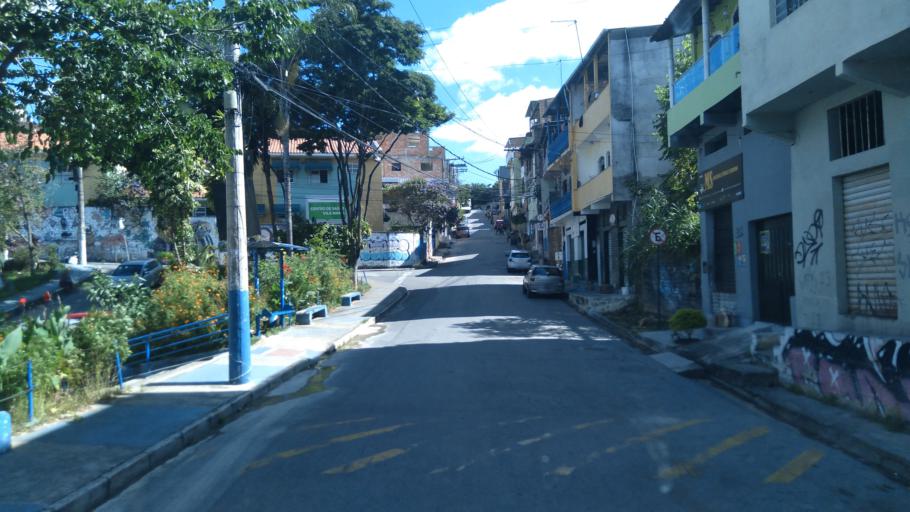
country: BR
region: Minas Gerais
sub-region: Belo Horizonte
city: Belo Horizonte
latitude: -19.8520
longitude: -43.8853
